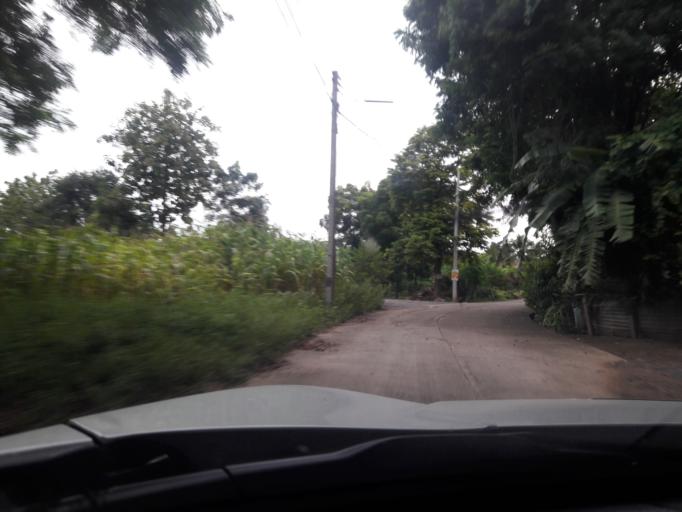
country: TH
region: Lop Buri
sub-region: Amphoe Tha Luang
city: Tha Luang
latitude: 15.0673
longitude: 101.1048
